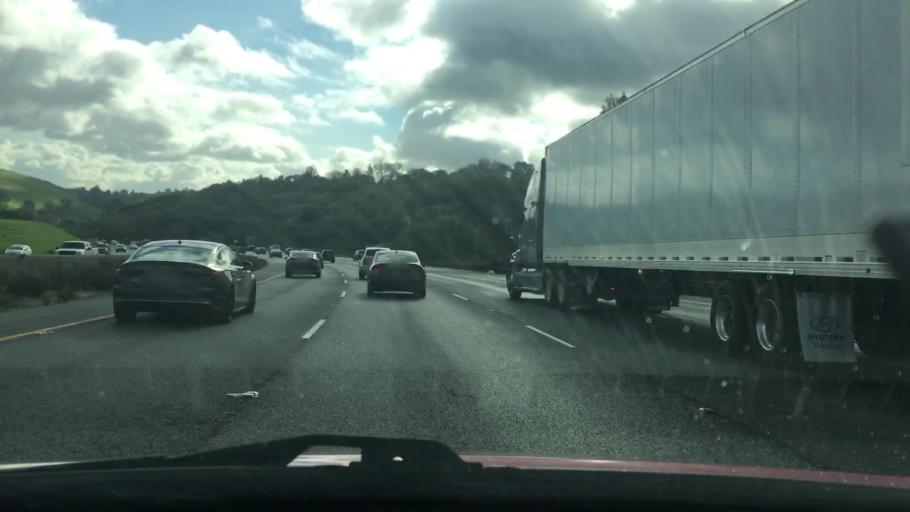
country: US
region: California
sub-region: San Mateo County
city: Ladera
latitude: 37.3943
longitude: -122.1746
